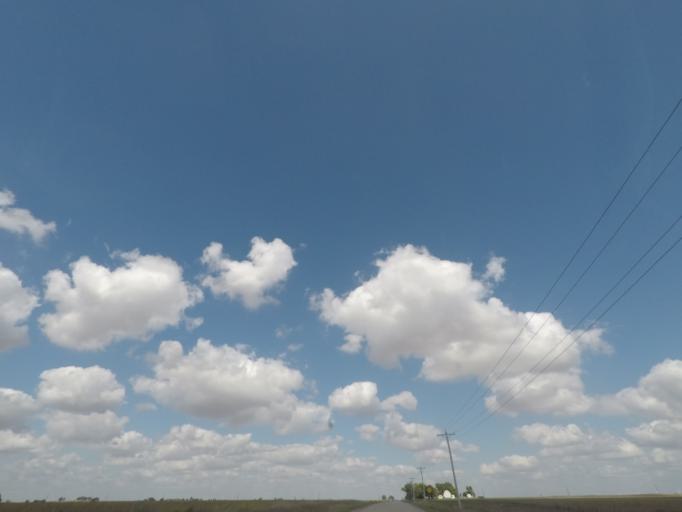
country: US
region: Iowa
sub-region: Story County
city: Nevada
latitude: 42.0755
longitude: -93.3863
